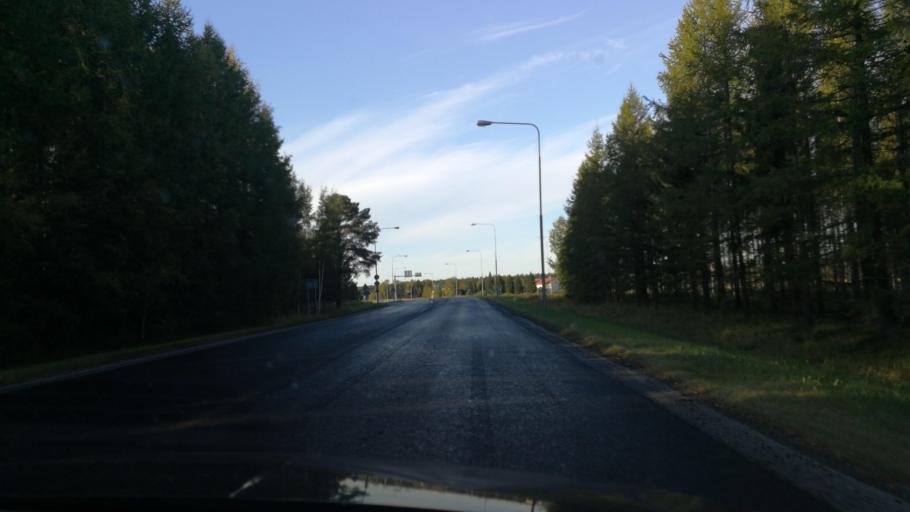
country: FI
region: Satakunta
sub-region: Pori
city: Luvia
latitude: 61.3372
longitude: 21.6592
